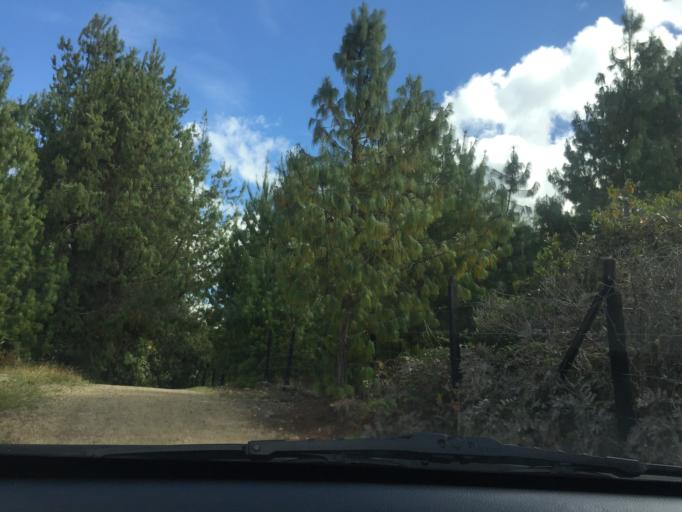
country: CO
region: Cundinamarca
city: Tocancipa
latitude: 4.9567
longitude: -73.8825
